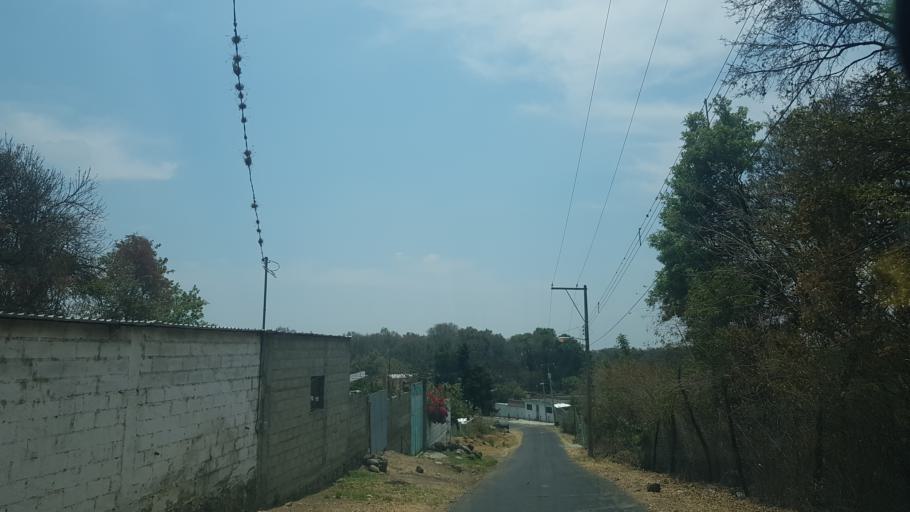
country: MX
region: Puebla
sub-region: Tochimilco
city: La Magdalena Yancuitlalpan
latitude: 18.8881
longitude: -98.6024
